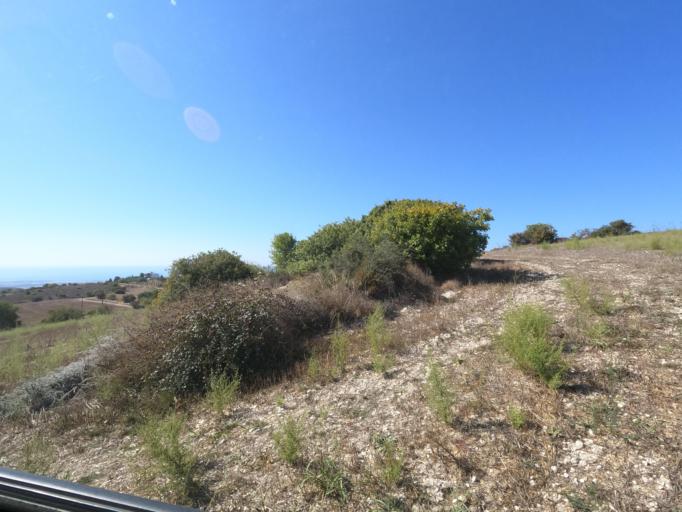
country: CY
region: Pafos
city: Mesogi
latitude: 34.8095
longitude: 32.4909
